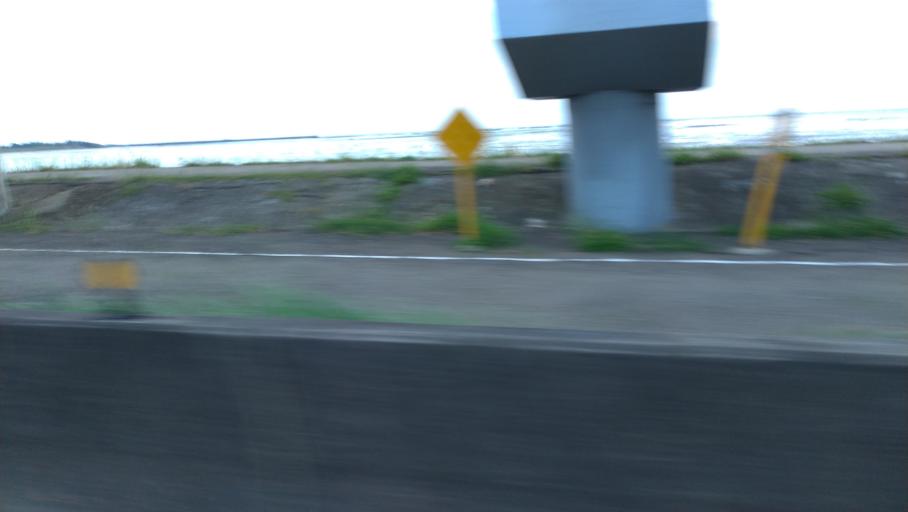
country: TW
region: Taiwan
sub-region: Hsinchu
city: Hsinchu
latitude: 24.7706
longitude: 120.9136
